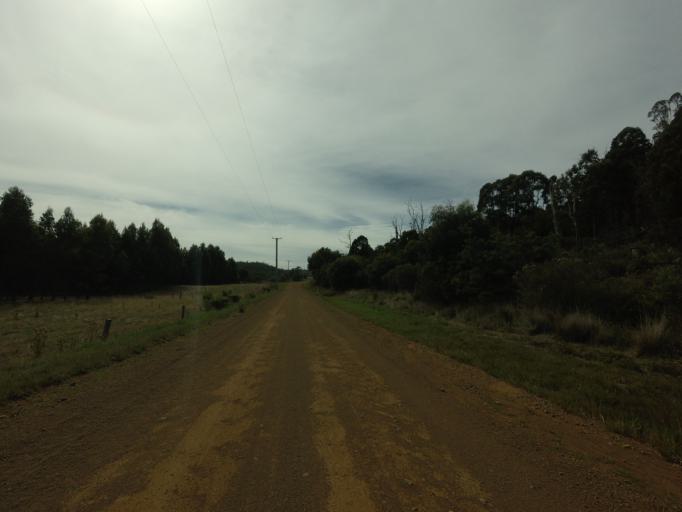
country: AU
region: Tasmania
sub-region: Sorell
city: Sorell
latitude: -42.4769
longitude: 147.5921
